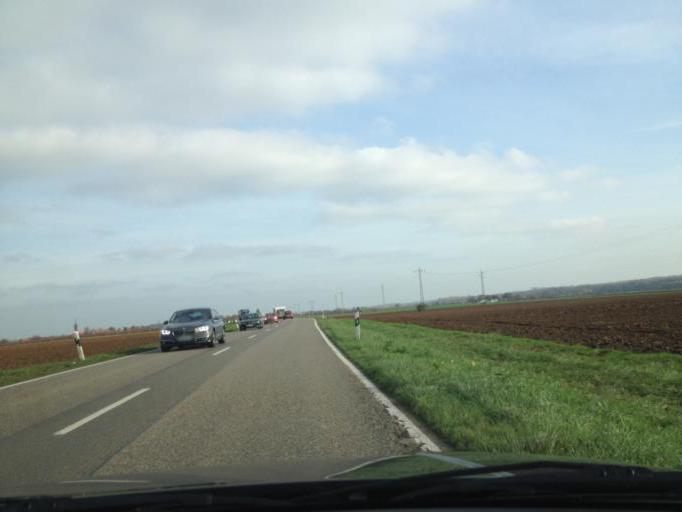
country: DE
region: Rheinland-Pfalz
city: Essingen
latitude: 49.2331
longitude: 8.1887
